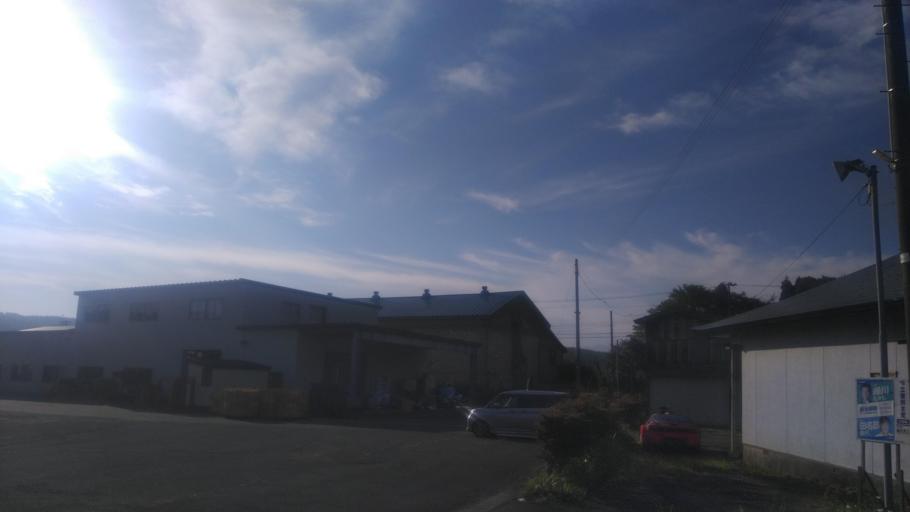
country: JP
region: Akita
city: Takanosu
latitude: 40.2566
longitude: 140.3975
